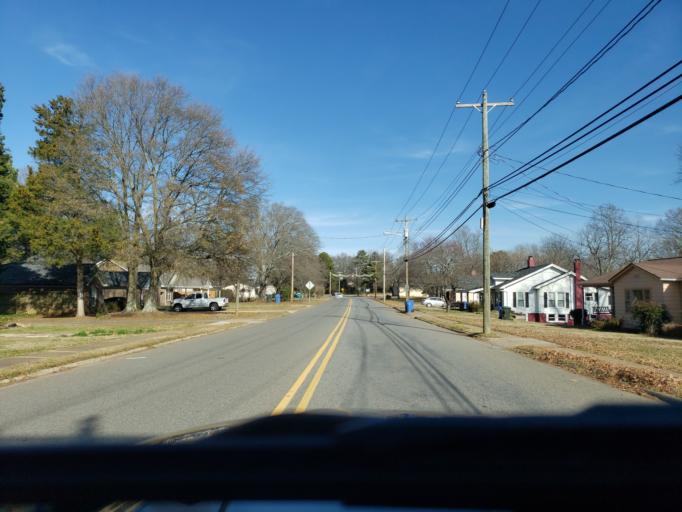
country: US
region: North Carolina
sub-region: Cleveland County
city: Kings Mountain
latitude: 35.2546
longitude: -81.3385
